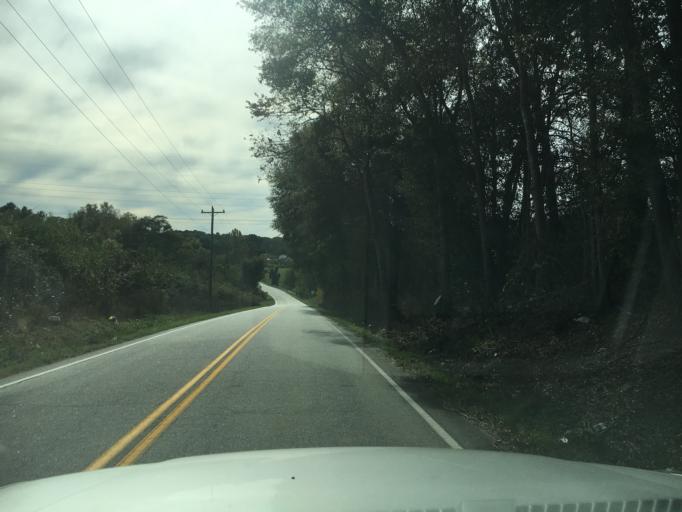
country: US
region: South Carolina
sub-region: Spartanburg County
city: Duncan
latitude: 34.9310
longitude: -82.1491
